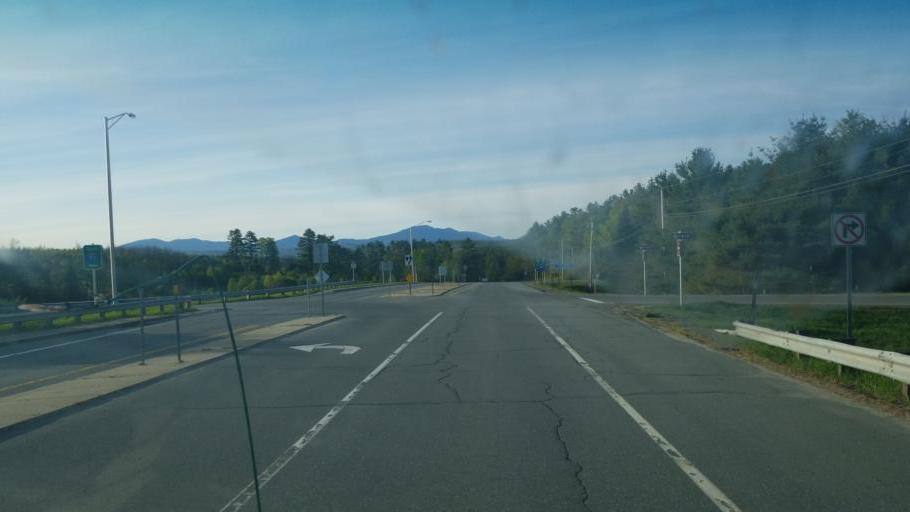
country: US
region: New Hampshire
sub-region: Grafton County
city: Littleton
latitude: 44.3248
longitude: -71.8059
